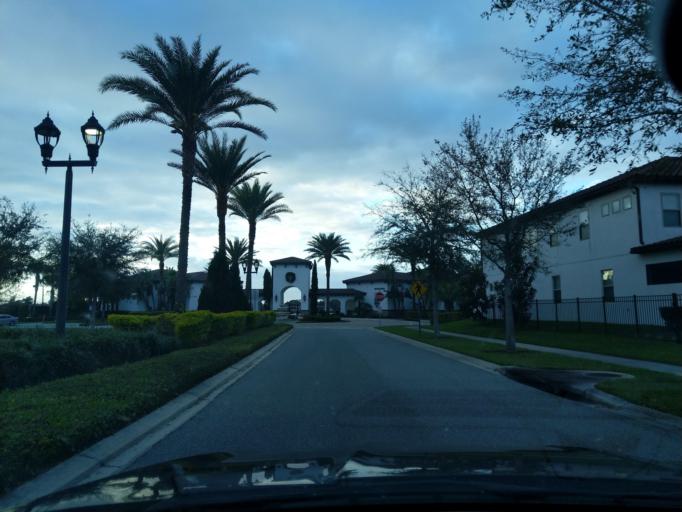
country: US
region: Florida
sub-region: Orange County
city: Williamsburg
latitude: 28.3946
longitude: -81.4939
